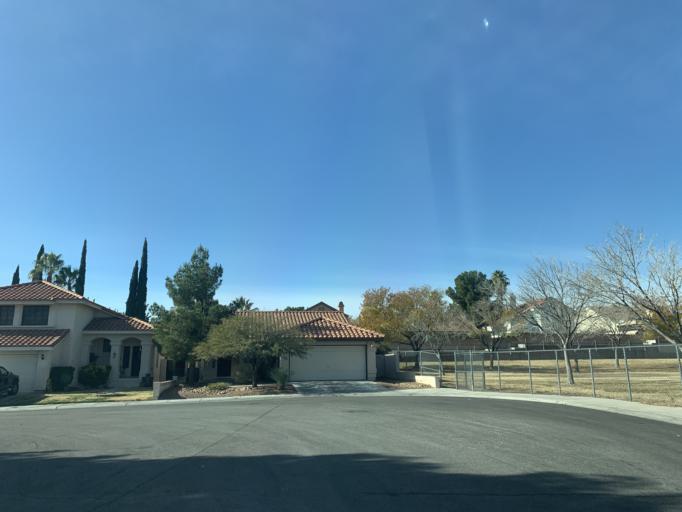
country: US
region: Nevada
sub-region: Clark County
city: Summerlin South
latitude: 36.1361
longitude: -115.2950
